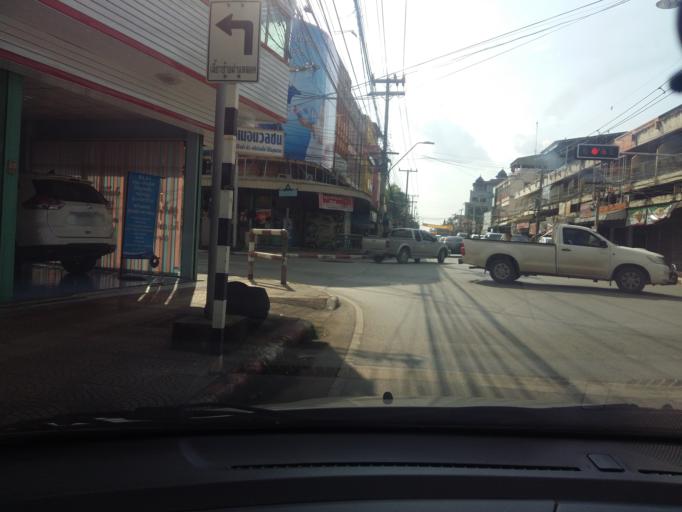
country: TH
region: Lampang
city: Lampang
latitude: 18.2845
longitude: 99.4996
